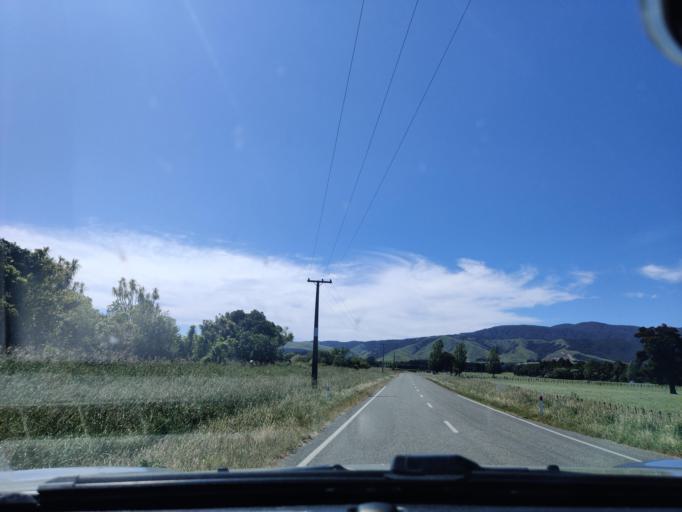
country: NZ
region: Wellington
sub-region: Upper Hutt City
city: Upper Hutt
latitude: -41.2877
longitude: 175.2686
